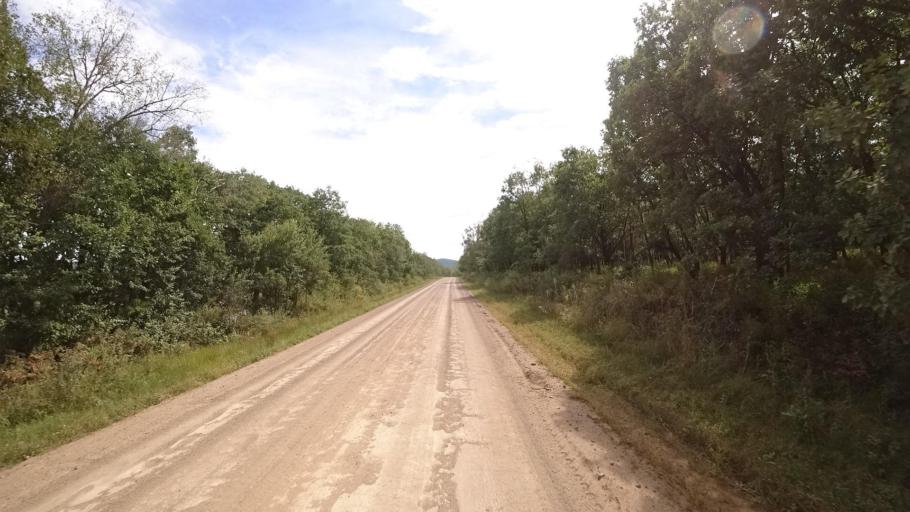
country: RU
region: Primorskiy
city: Yakovlevka
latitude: 44.6009
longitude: 133.6045
